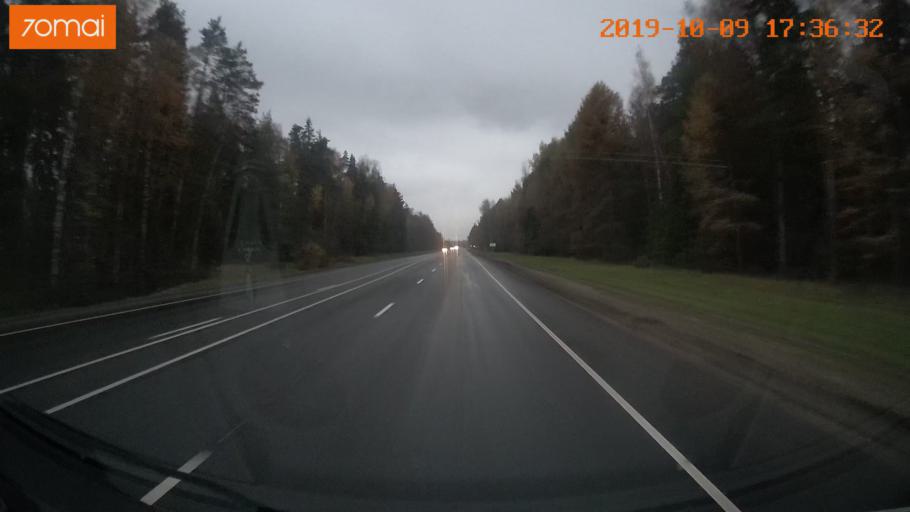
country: RU
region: Ivanovo
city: Bogorodskoye
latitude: 57.0770
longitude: 40.9960
